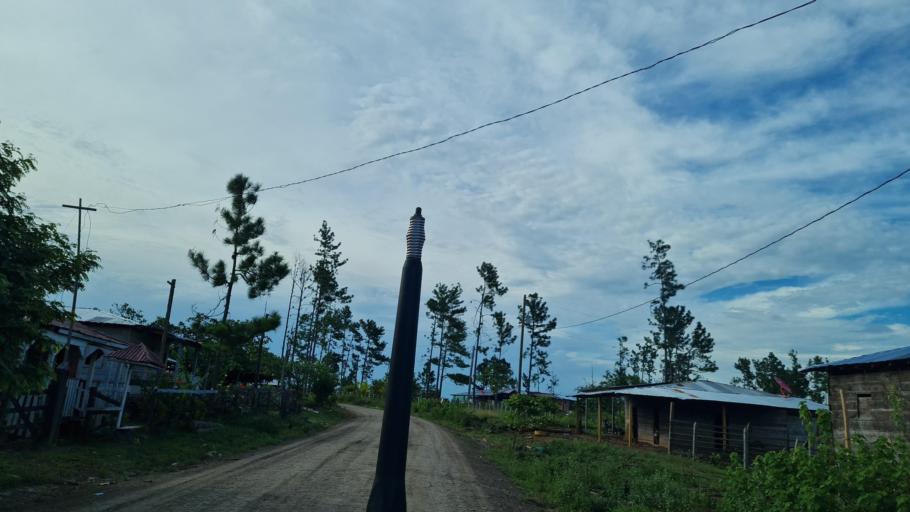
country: NI
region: Atlantico Sur
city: La Cruz de Rio Grande
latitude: 13.5649
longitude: -84.3142
